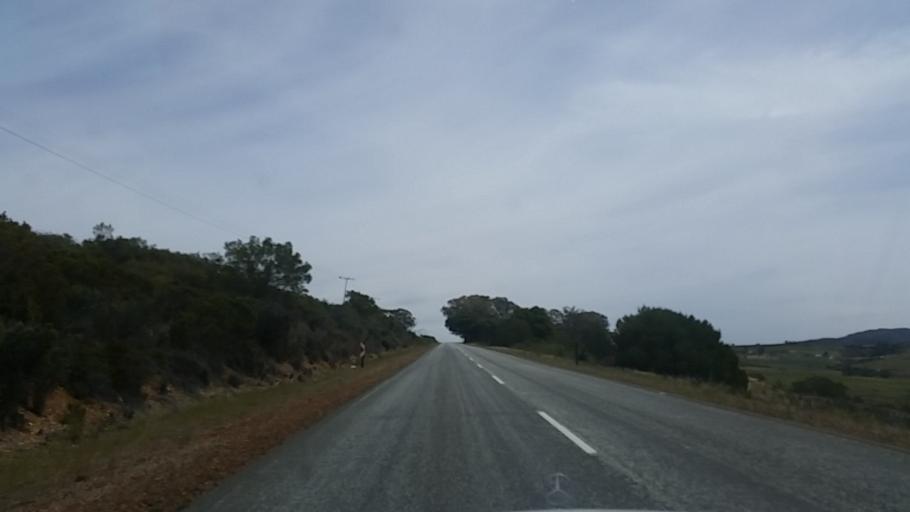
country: ZA
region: Western Cape
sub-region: Eden District Municipality
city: Knysna
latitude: -33.7728
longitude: 22.9248
